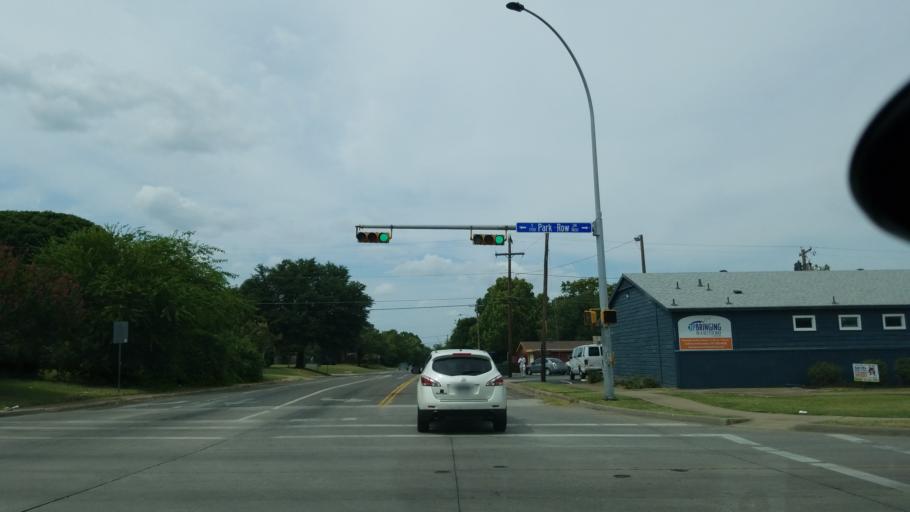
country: US
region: Texas
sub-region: Tarrant County
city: Arlington
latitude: 32.7209
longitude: -97.0833
